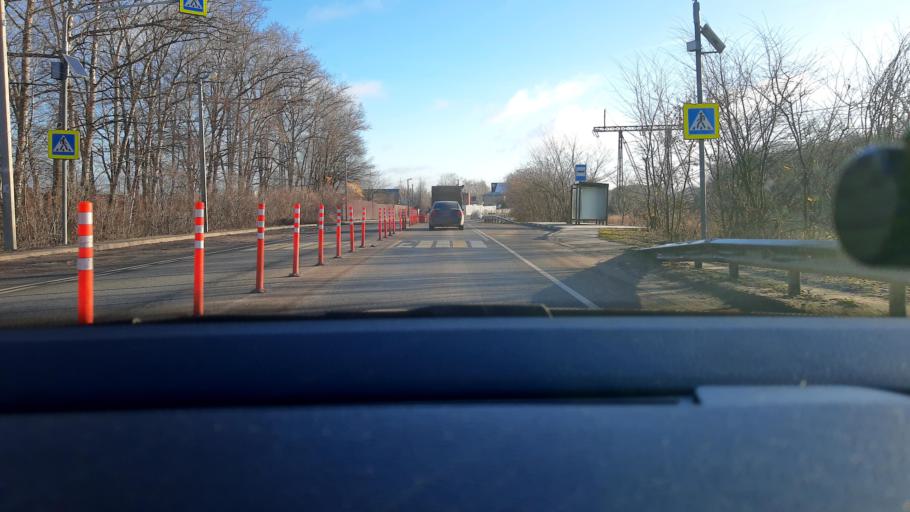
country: RU
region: Moskovskaya
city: Pirogovskiy
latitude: 55.9701
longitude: 37.6965
